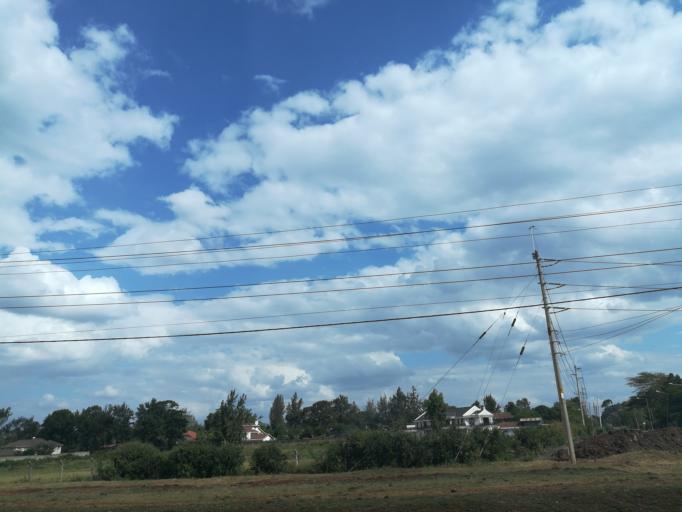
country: KE
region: Nairobi Area
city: Nairobi
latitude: -1.3249
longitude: 36.7564
